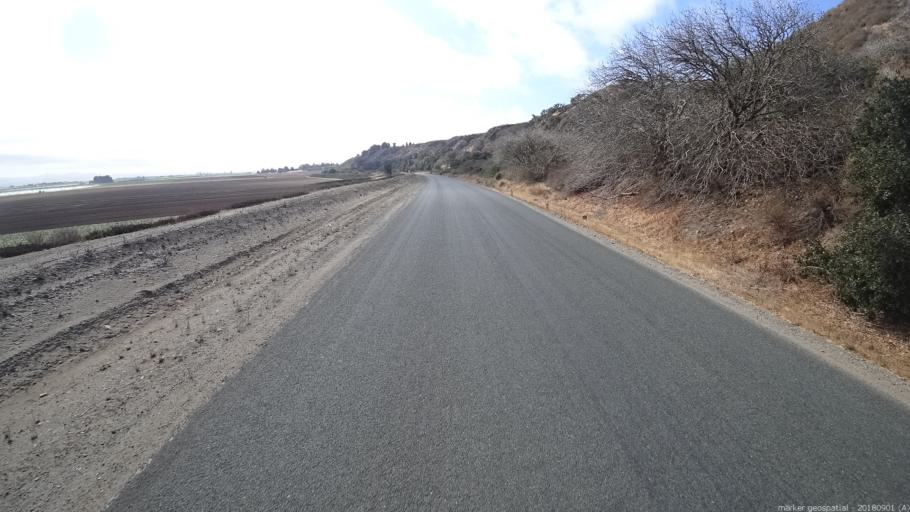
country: US
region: California
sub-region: Monterey County
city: Soledad
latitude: 36.4026
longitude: -121.3793
